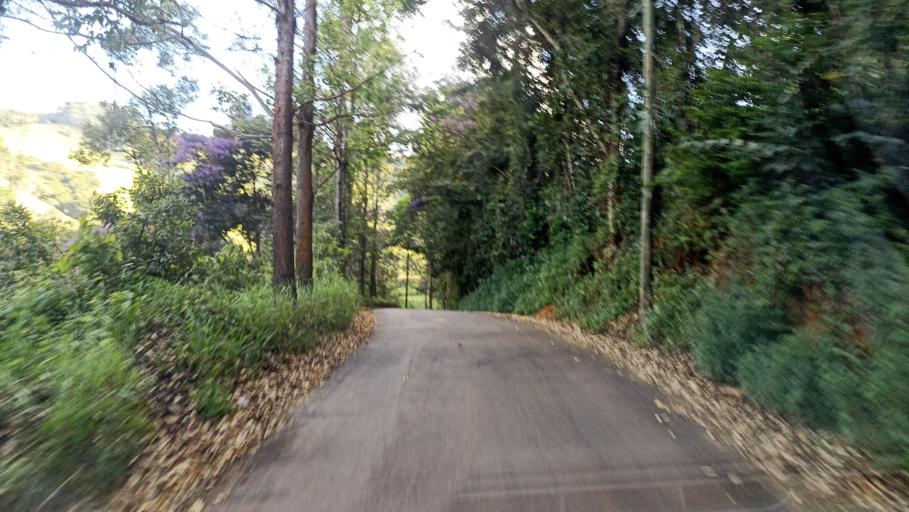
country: BR
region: Minas Gerais
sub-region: Ouro Preto
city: Ouro Preto
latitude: -20.3120
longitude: -43.5888
